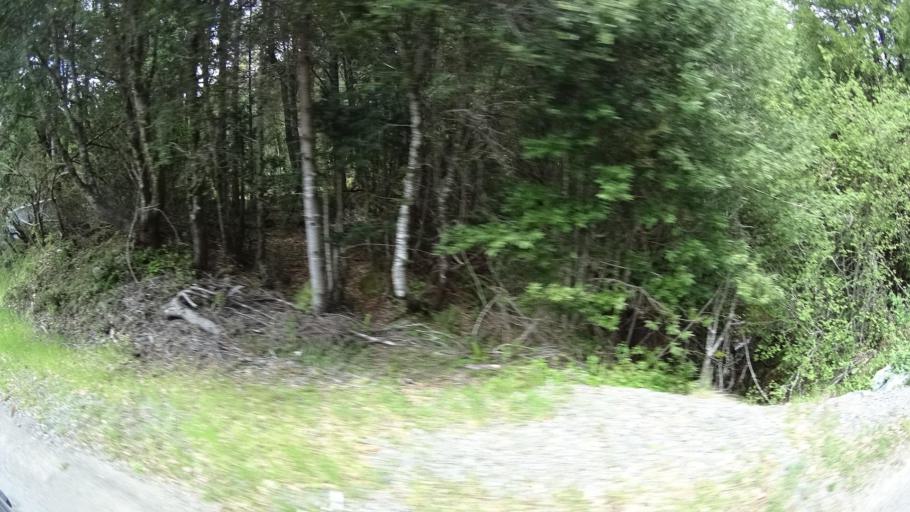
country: US
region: California
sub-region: Humboldt County
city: Redway
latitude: 40.0444
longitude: -123.9582
